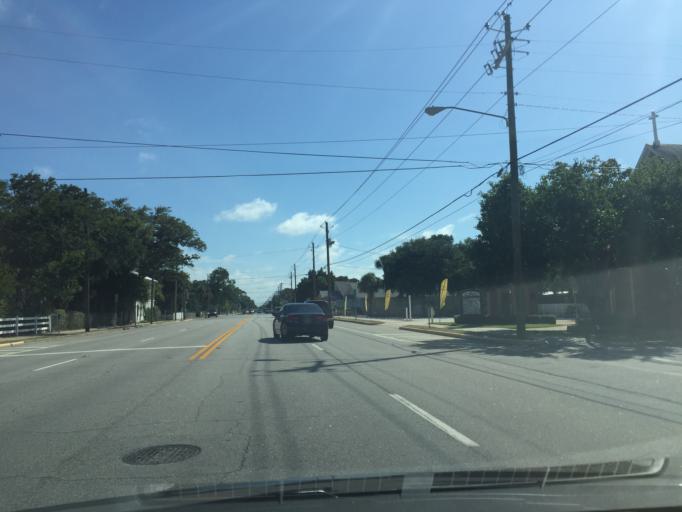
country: US
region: Georgia
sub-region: Chatham County
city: Tybee Island
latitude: 32.0038
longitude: -80.8447
